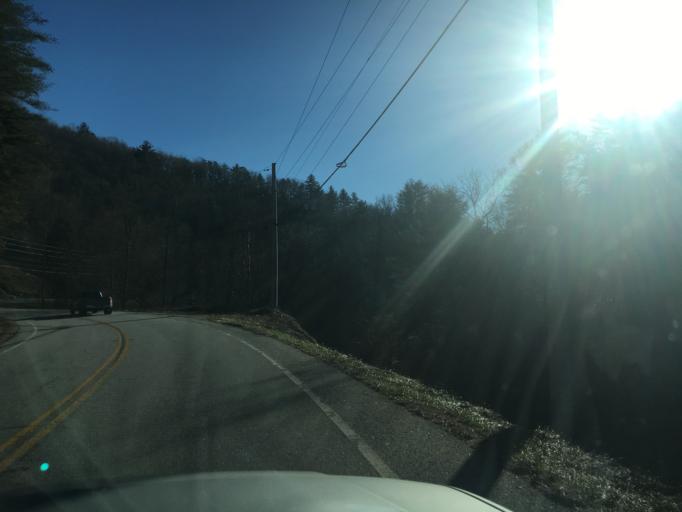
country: US
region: Georgia
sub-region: Union County
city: Blairsville
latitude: 34.7850
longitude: -83.9069
